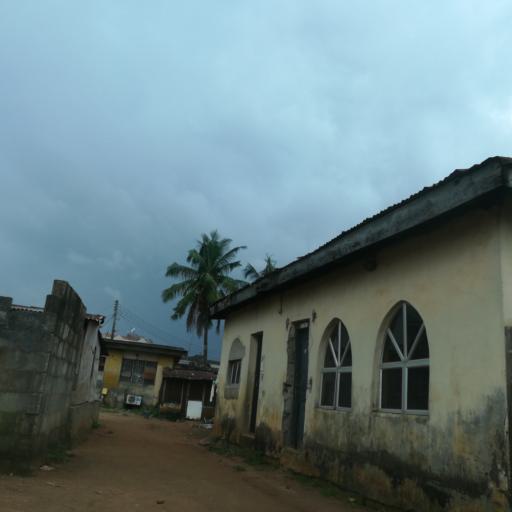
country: NG
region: Lagos
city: Agege
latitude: 6.6053
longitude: 3.2958
